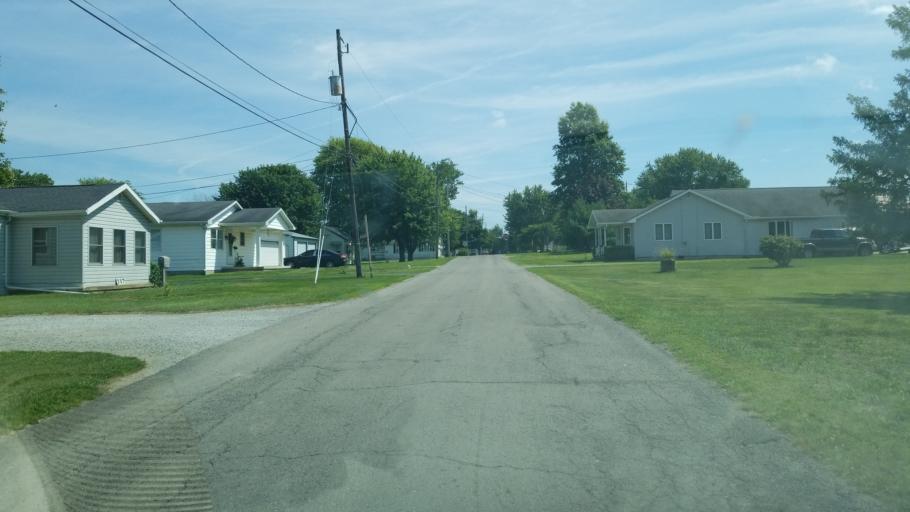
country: US
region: Ohio
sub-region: Hardin County
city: Kenton
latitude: 40.6411
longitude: -83.5993
